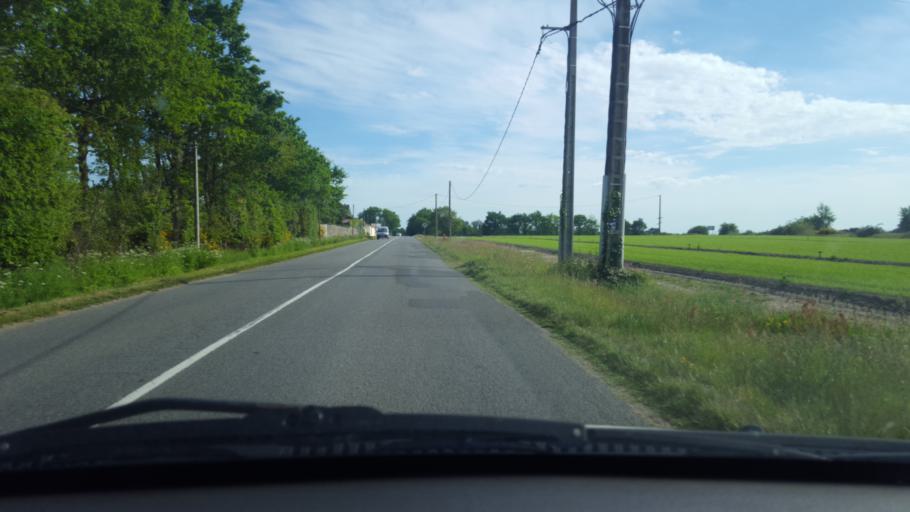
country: FR
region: Pays de la Loire
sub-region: Departement de la Loire-Atlantique
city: La Chevroliere
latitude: 47.0747
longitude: -1.5667
